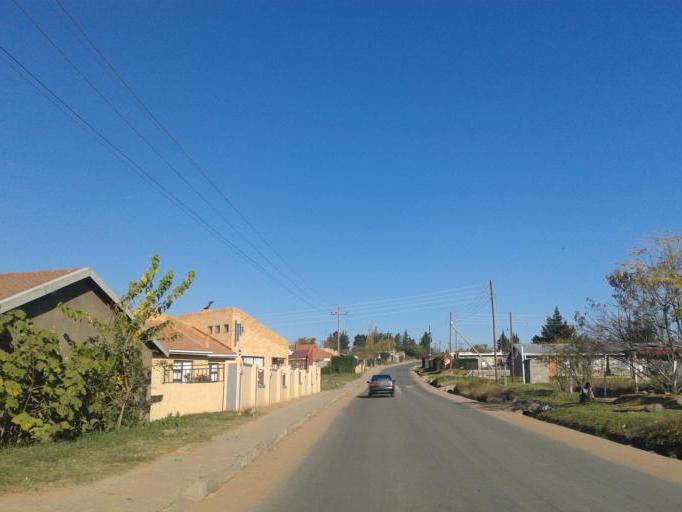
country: LS
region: Maseru
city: Maseru
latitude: -29.2790
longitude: 27.5343
